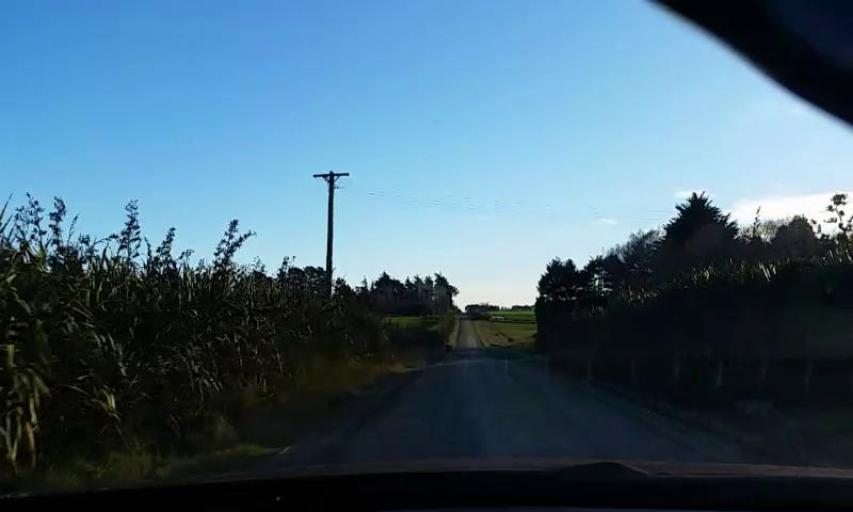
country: NZ
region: Southland
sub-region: Invercargill City
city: Invercargill
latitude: -46.2850
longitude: 168.5145
